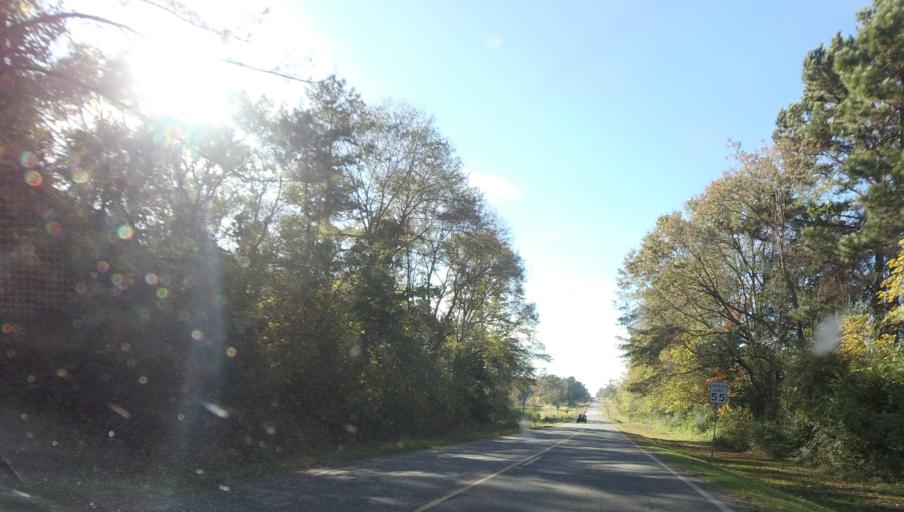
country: US
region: Georgia
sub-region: Talbot County
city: Talbotton
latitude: 32.6806
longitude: -84.5620
